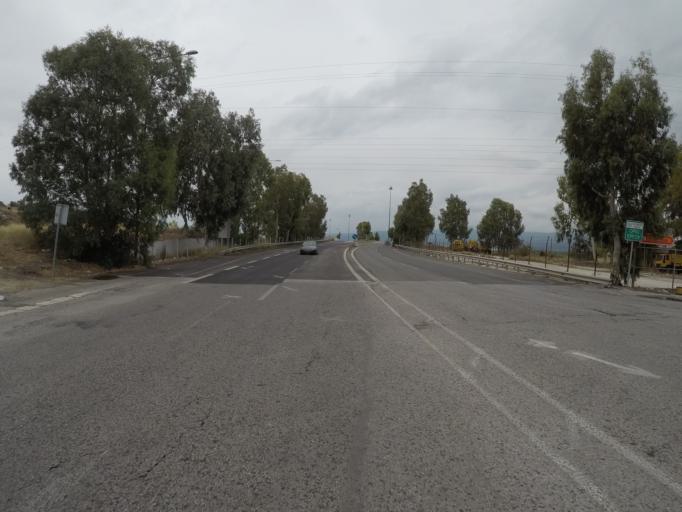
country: GR
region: Peloponnese
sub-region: Nomos Korinthias
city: Isthmia
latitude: 37.9270
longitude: 22.9977
